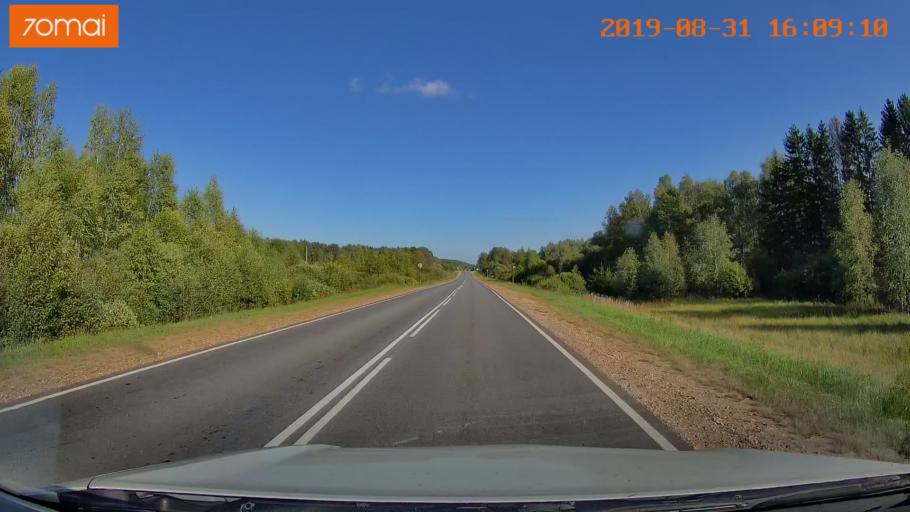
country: RU
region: Kaluga
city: Yukhnov
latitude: 54.5895
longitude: 35.3916
